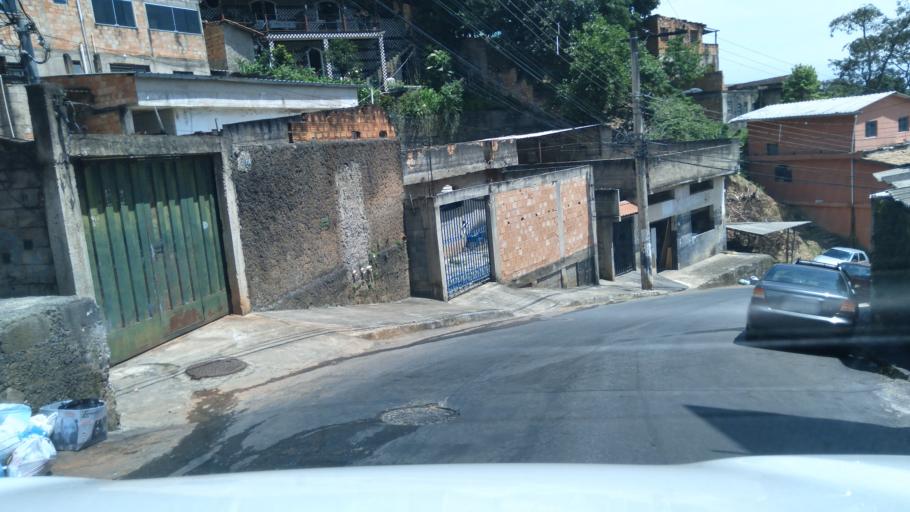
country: BR
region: Minas Gerais
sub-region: Contagem
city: Contagem
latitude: -19.9165
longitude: -44.0249
